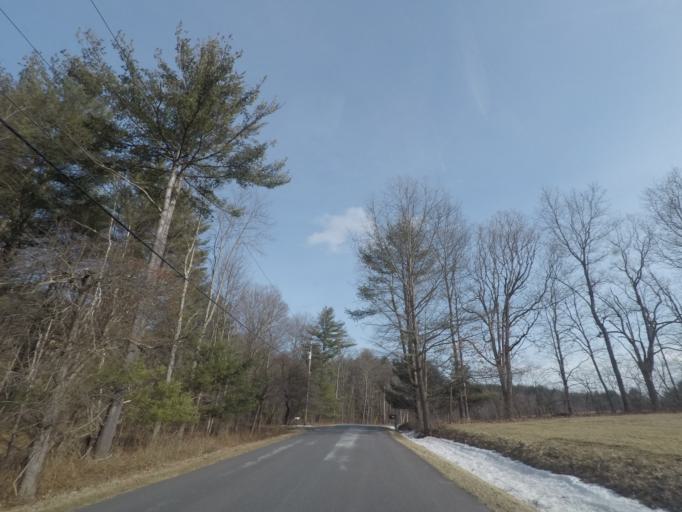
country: US
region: New York
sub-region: Rensselaer County
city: Nassau
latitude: 42.5066
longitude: -73.5556
